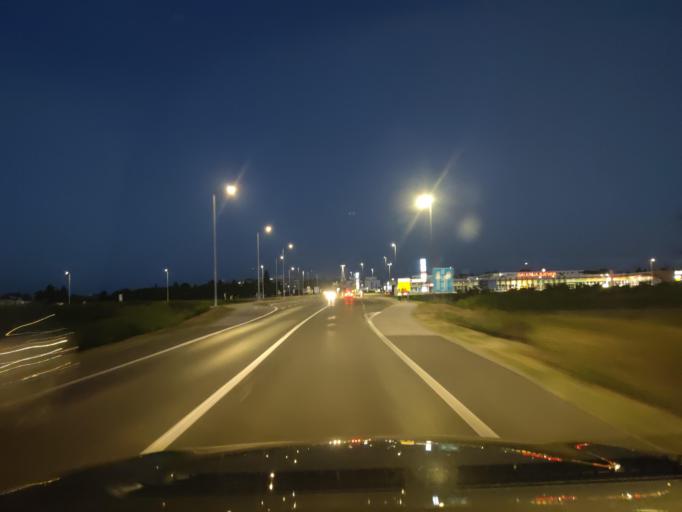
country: HR
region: Medimurska
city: Senkovec
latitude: 46.3985
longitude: 16.4271
